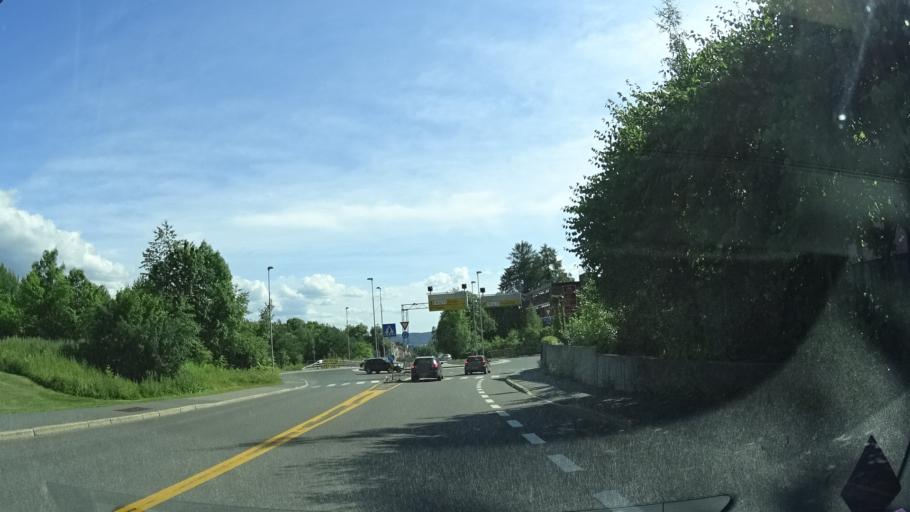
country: NO
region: Oslo
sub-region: Oslo
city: Oslo
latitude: 59.9541
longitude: 10.7608
